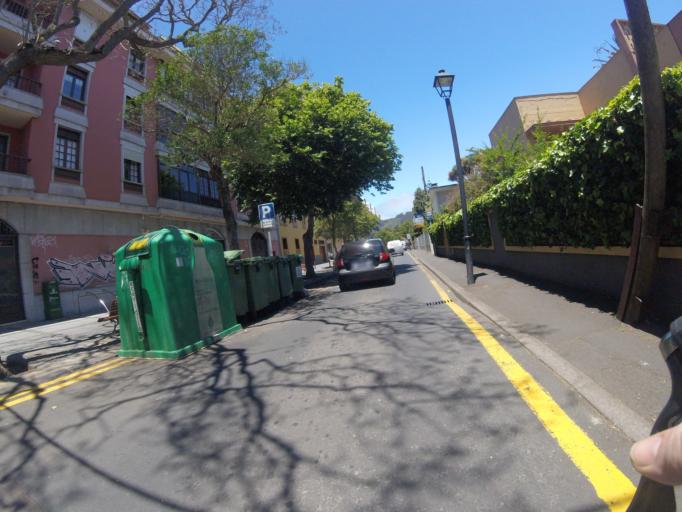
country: ES
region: Canary Islands
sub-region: Provincia de Santa Cruz de Tenerife
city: La Laguna
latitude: 28.4912
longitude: -16.3196
